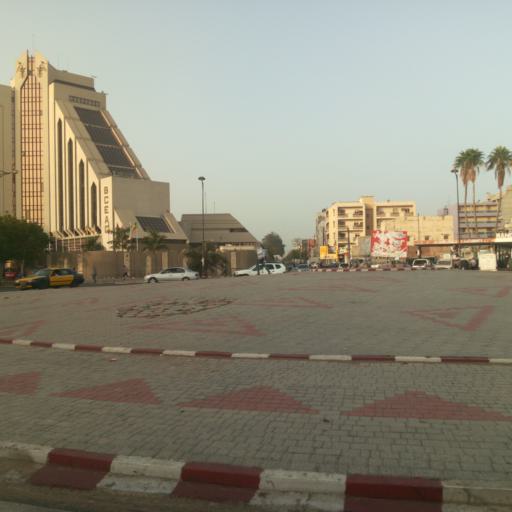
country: SN
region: Dakar
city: Dakar
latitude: 14.6836
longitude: -17.4444
